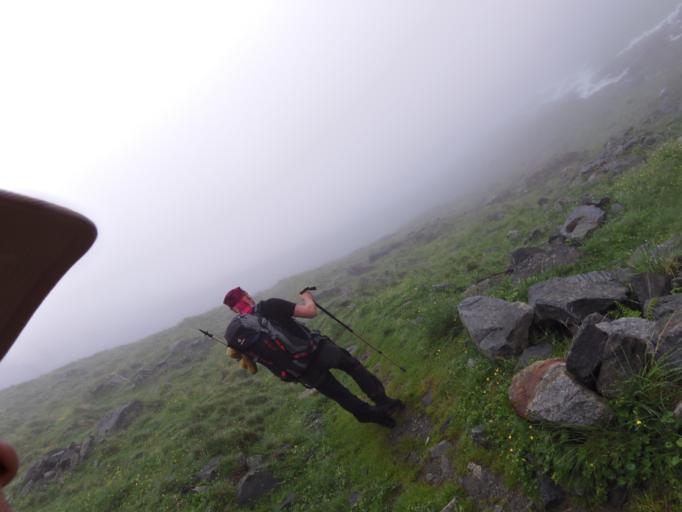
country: AT
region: Tyrol
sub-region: Politischer Bezirk Innsbruck Land
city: Neustift im Stubaital
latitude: 47.0573
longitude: 11.2080
